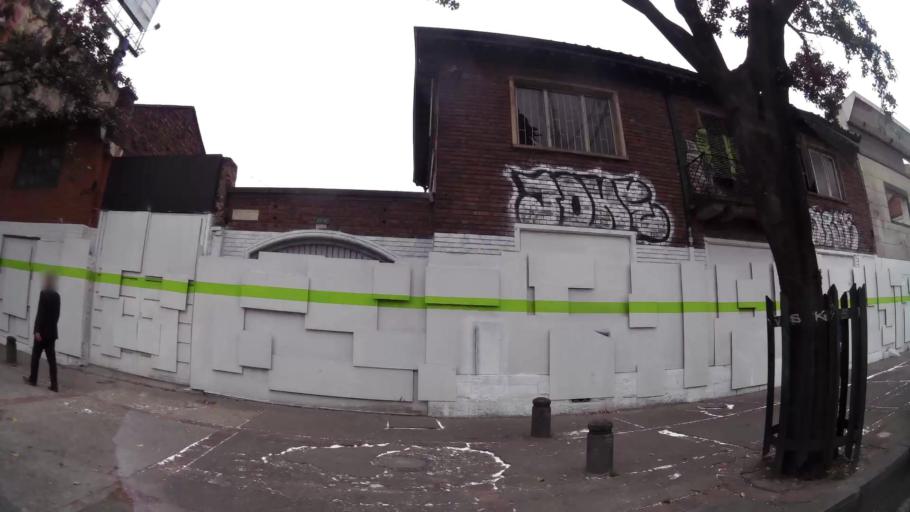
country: CO
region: Bogota D.C.
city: Bogota
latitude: 4.6216
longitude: -74.0696
